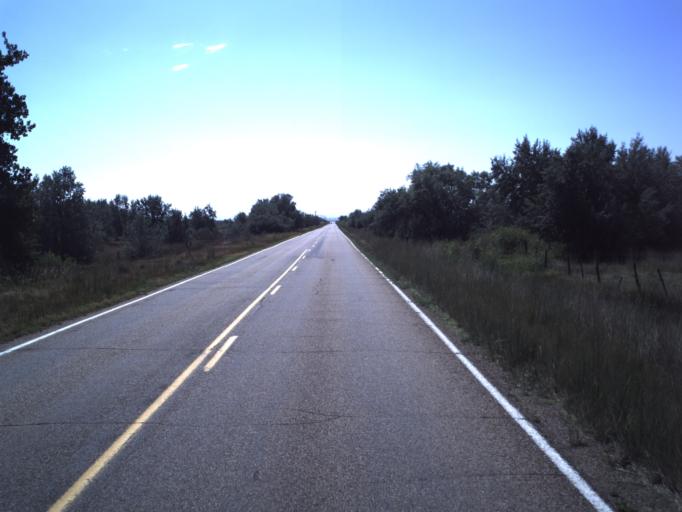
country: US
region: Utah
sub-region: Duchesne County
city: Duchesne
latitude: 40.3230
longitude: -110.2615
